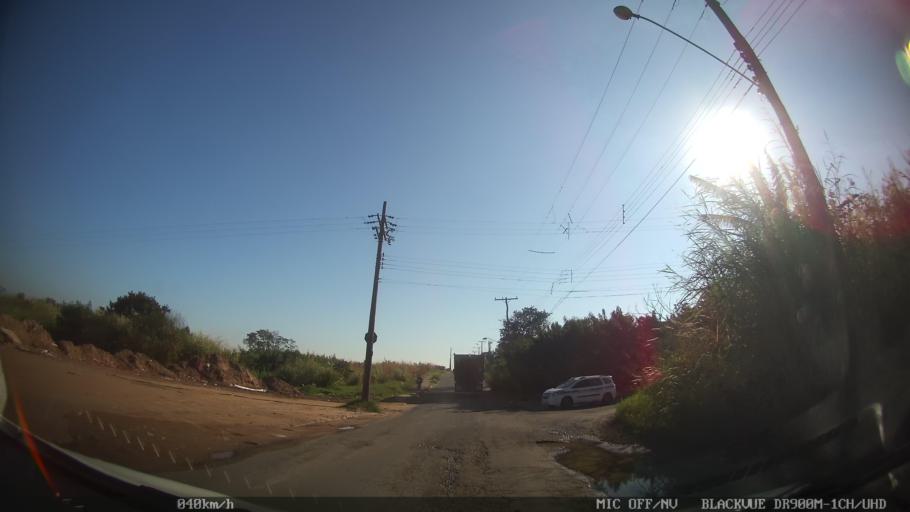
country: BR
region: Sao Paulo
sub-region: Campinas
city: Campinas
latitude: -22.9815
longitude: -47.1094
